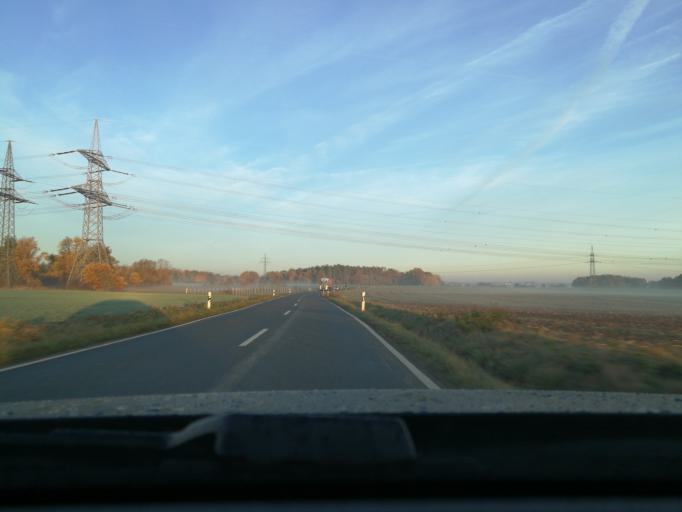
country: DE
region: Bavaria
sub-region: Regierungsbezirk Mittelfranken
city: Obermichelbach
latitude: 49.5496
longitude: 10.9261
